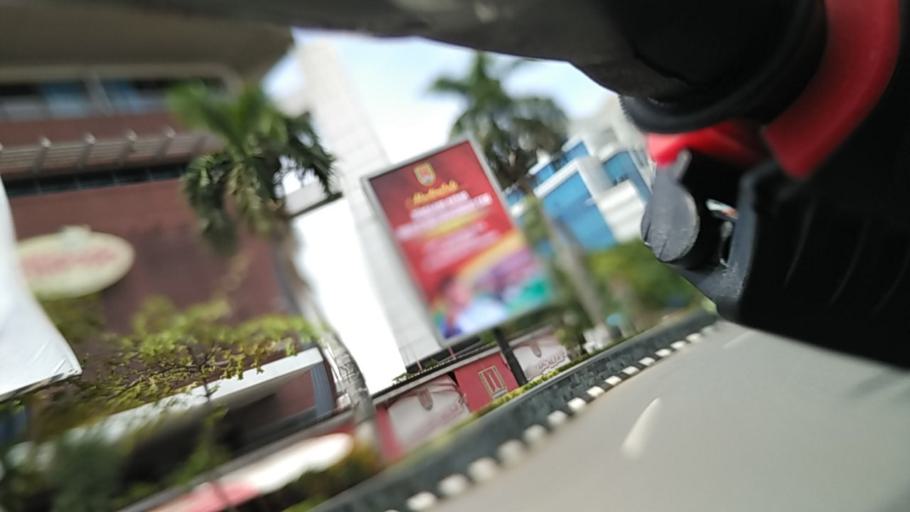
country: ID
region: Central Java
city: Semarang
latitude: -6.9919
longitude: 110.4230
